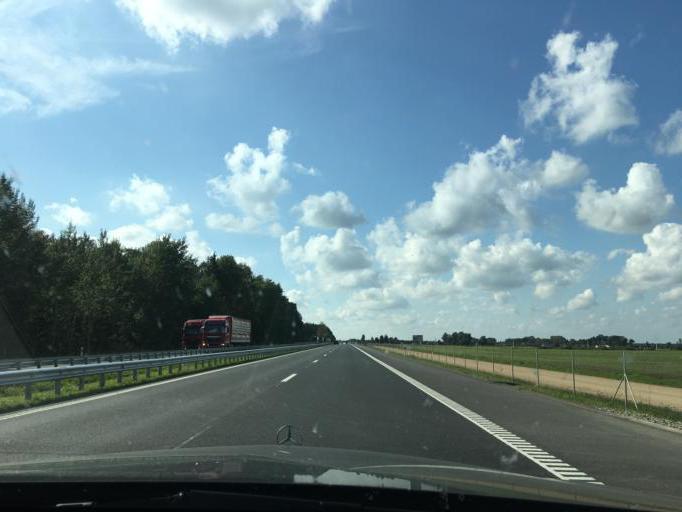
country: LT
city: Kazlu Ruda
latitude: 54.6750
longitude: 23.5580
